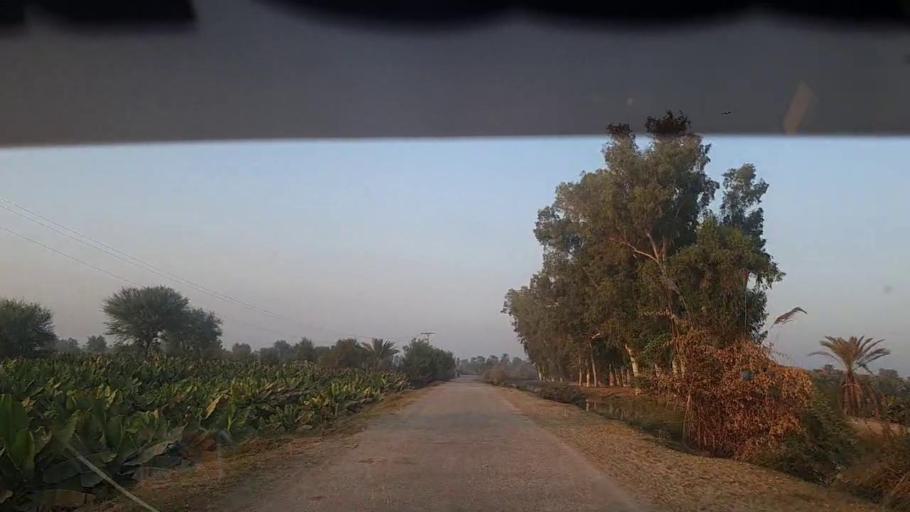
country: PK
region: Sindh
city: Ranipur
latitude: 27.2359
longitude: 68.5492
